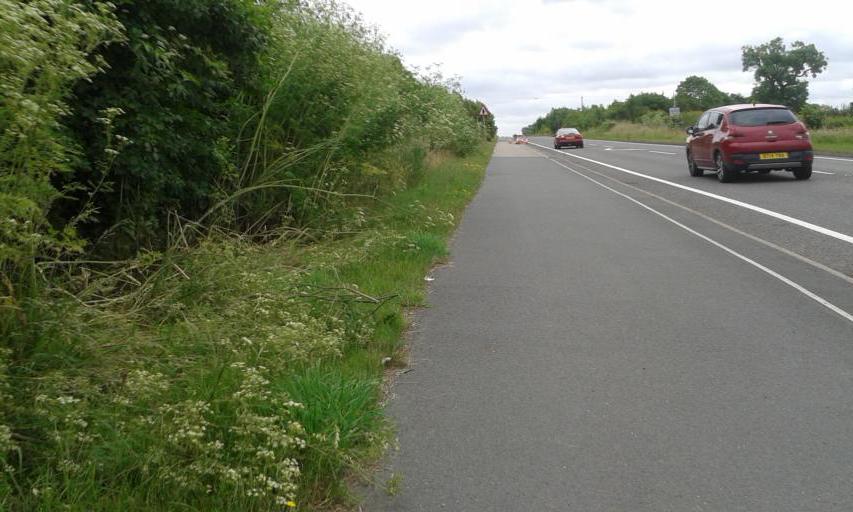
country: GB
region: England
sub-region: Leicestershire
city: Earl Shilton
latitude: 52.5671
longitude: -1.3106
